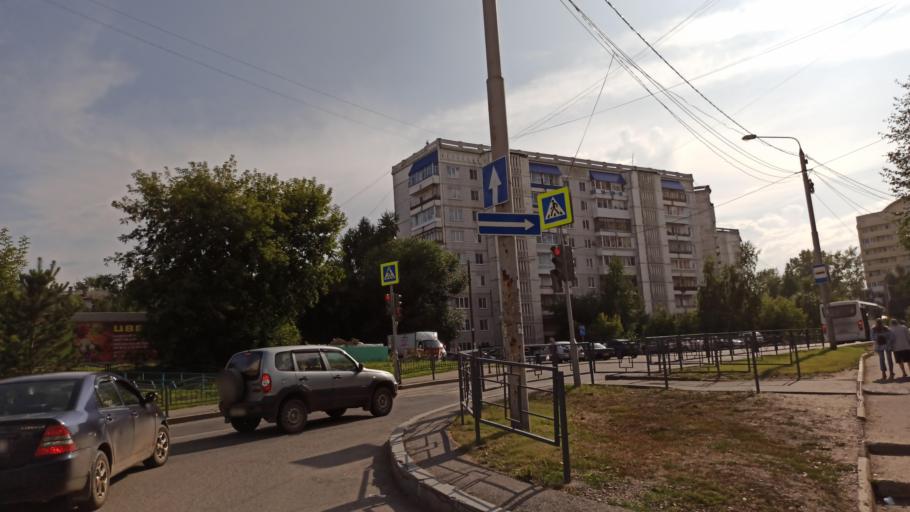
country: RU
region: Tomsk
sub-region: Tomskiy Rayon
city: Tomsk
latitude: 56.4825
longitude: 85.0059
